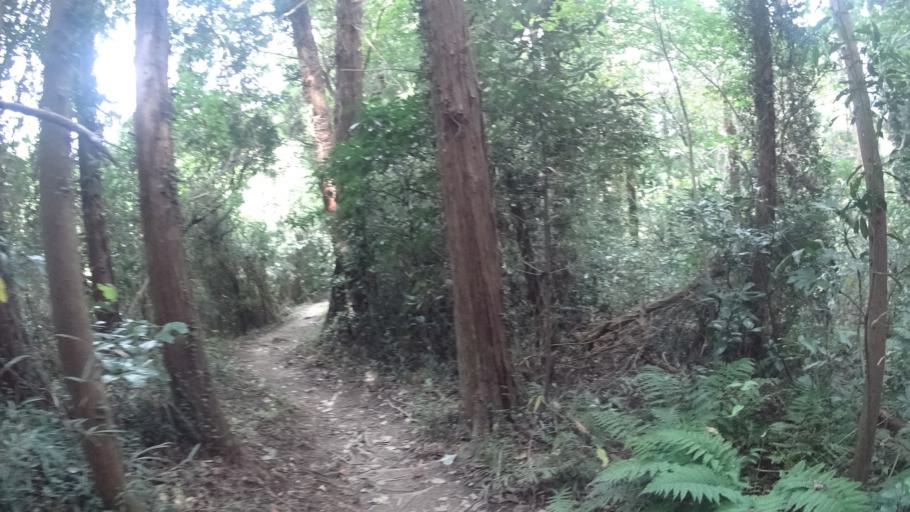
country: JP
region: Kanagawa
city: Zushi
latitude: 35.2929
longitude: 139.6029
